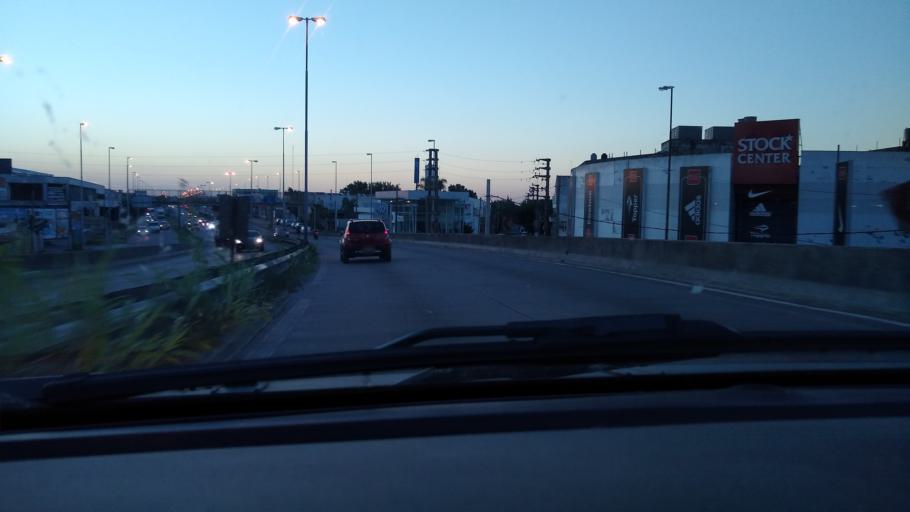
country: AR
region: Buenos Aires
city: San Justo
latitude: -34.6850
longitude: -58.5615
